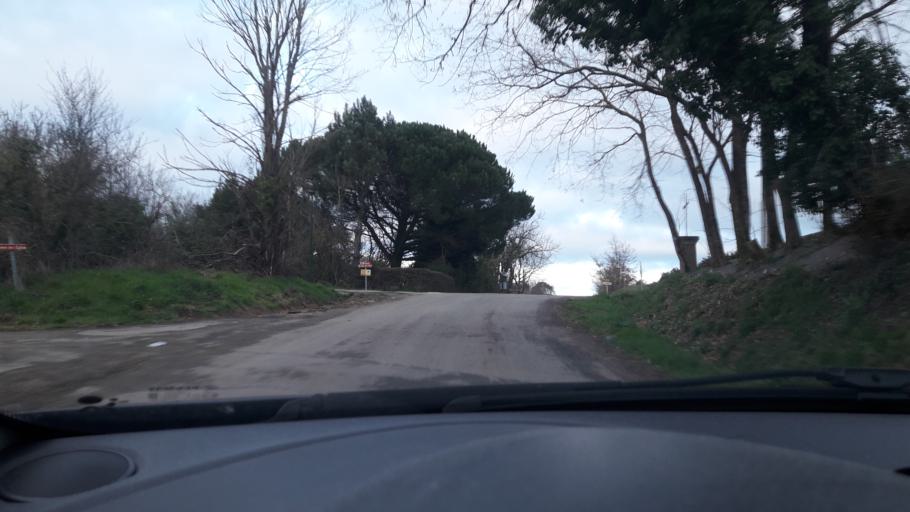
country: FR
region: Midi-Pyrenees
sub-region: Departement de la Haute-Garonne
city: Launac
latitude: 43.7221
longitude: 1.0998
